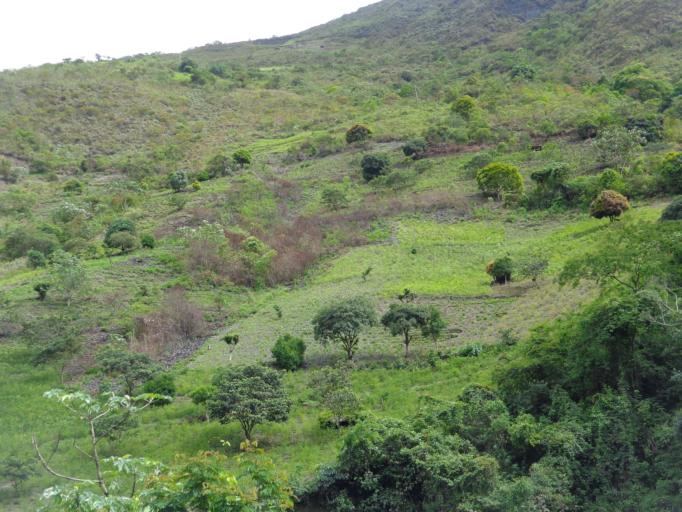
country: BO
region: La Paz
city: Coripata
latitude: -16.3961
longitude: -67.6294
